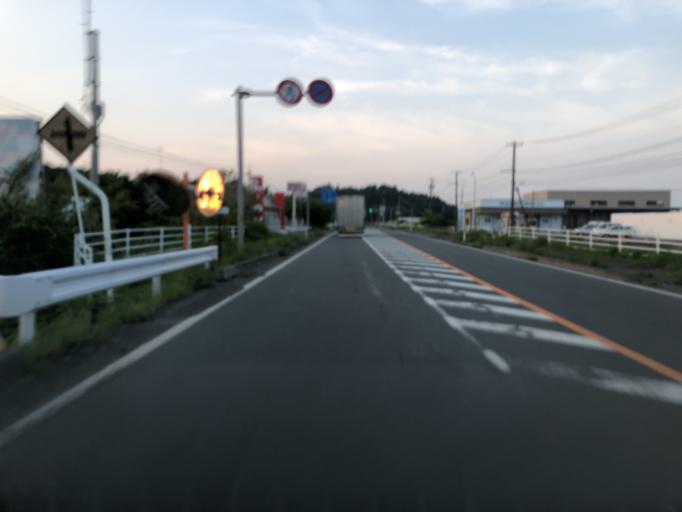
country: JP
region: Fukushima
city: Namie
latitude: 37.4561
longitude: 141.0101
